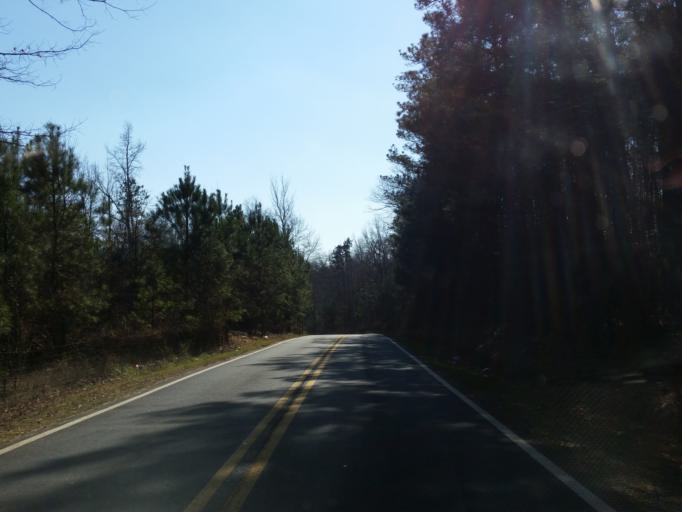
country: US
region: Georgia
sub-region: Henry County
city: Stockbridge
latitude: 33.4722
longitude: -84.2207
